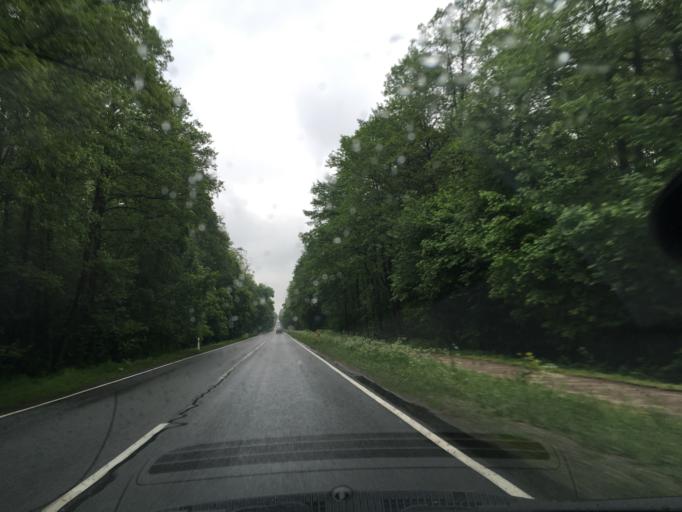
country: PL
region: Lublin Voivodeship
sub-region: Powiat rycki
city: Deblin
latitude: 51.5735
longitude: 21.8965
